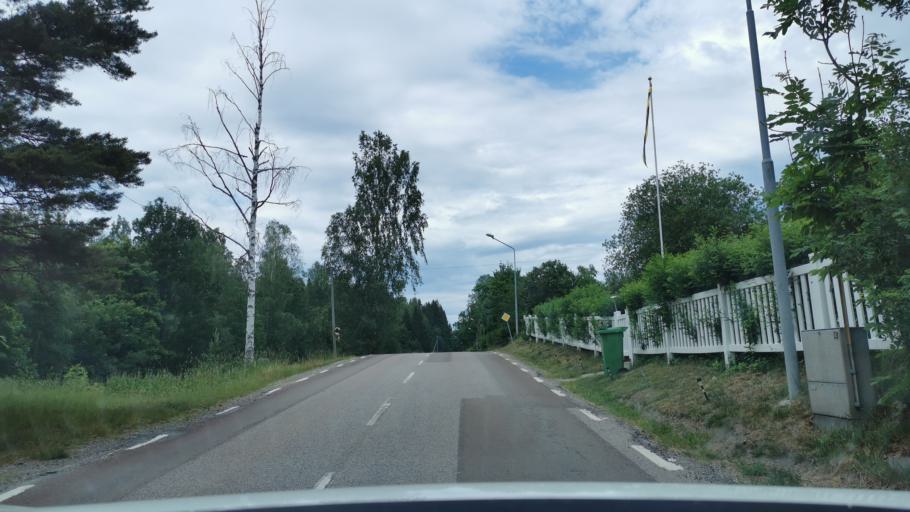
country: SE
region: Vaestra Goetaland
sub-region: Melleruds Kommun
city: Mellerud
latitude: 58.8268
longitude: 12.4135
